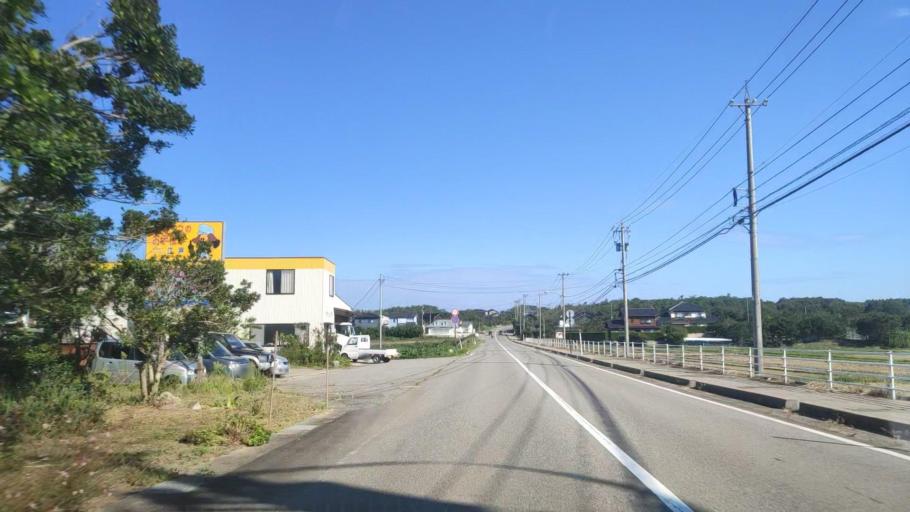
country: JP
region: Ishikawa
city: Hakui
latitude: 36.9825
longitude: 136.7761
